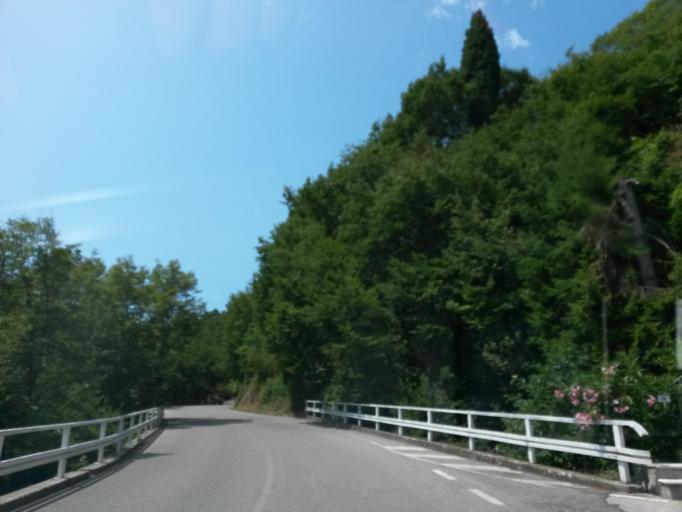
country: IT
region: Lombardy
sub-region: Provincia di Brescia
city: Gargnano
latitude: 45.6884
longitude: 10.6533
